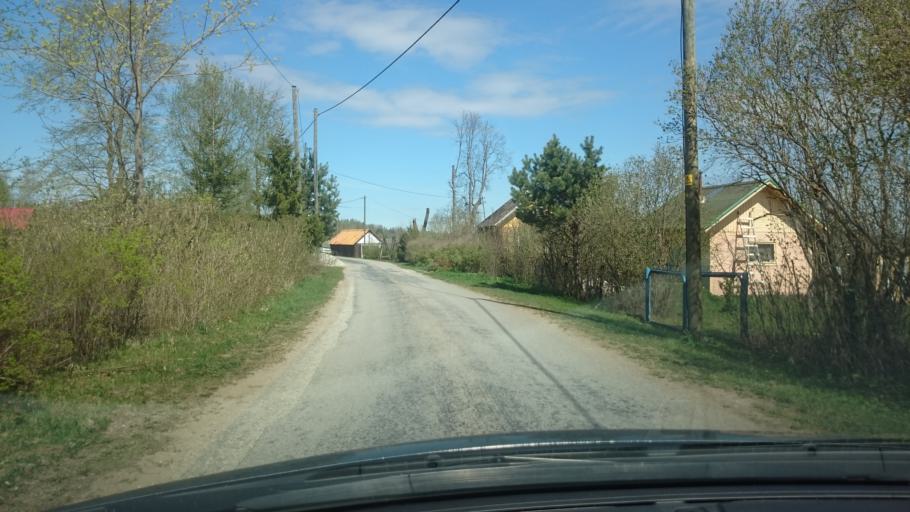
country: EE
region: Ida-Virumaa
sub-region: Sillamaee linn
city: Sillamae
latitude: 59.1243
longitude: 27.8031
